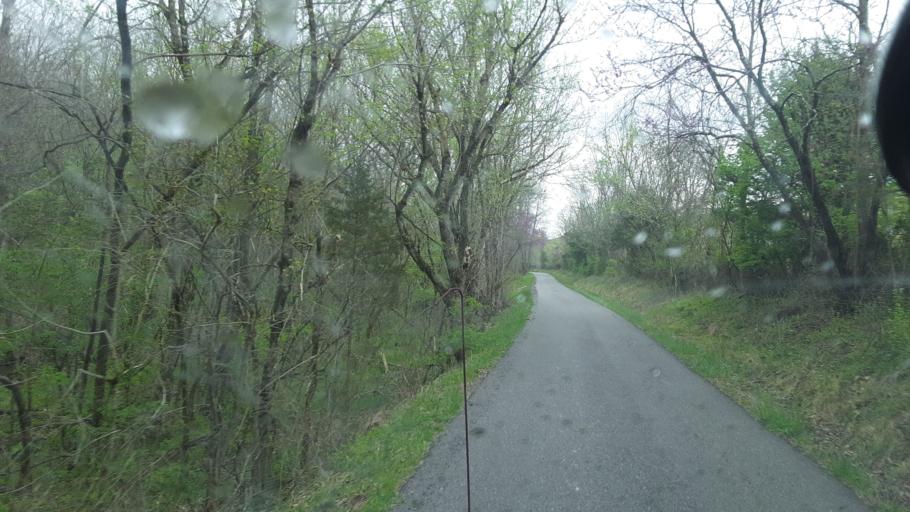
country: US
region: Kentucky
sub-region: Owen County
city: Owenton
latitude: 38.6434
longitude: -84.7818
